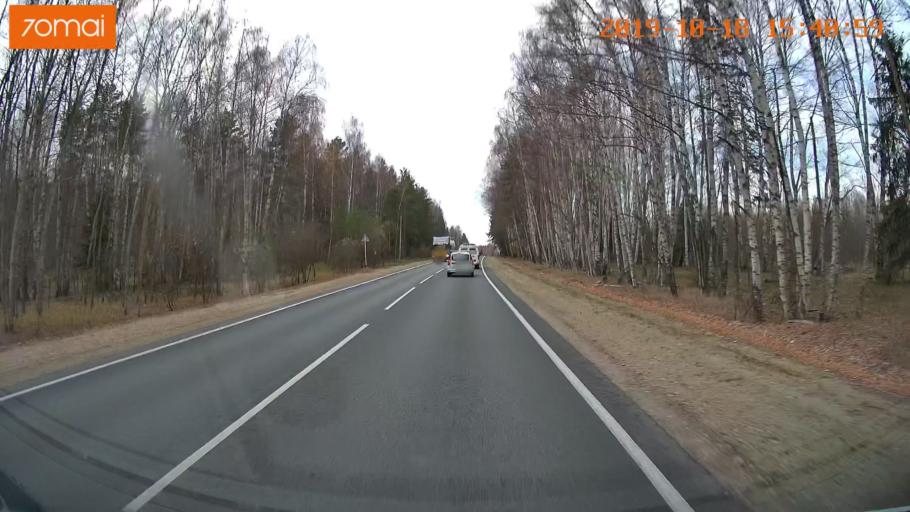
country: RU
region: Vladimir
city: Golovino
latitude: 55.9407
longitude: 40.5889
